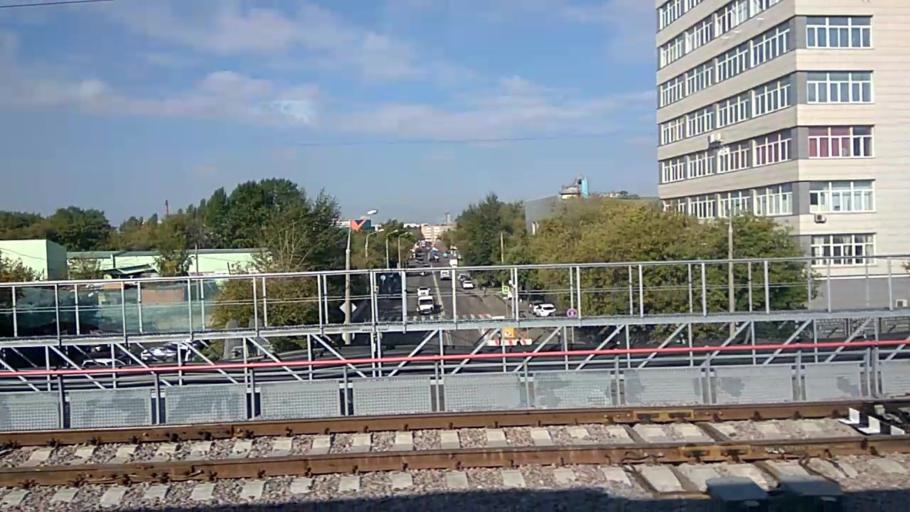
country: RU
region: Moscow
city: Ryazanskiy
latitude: 55.7360
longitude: 37.7307
